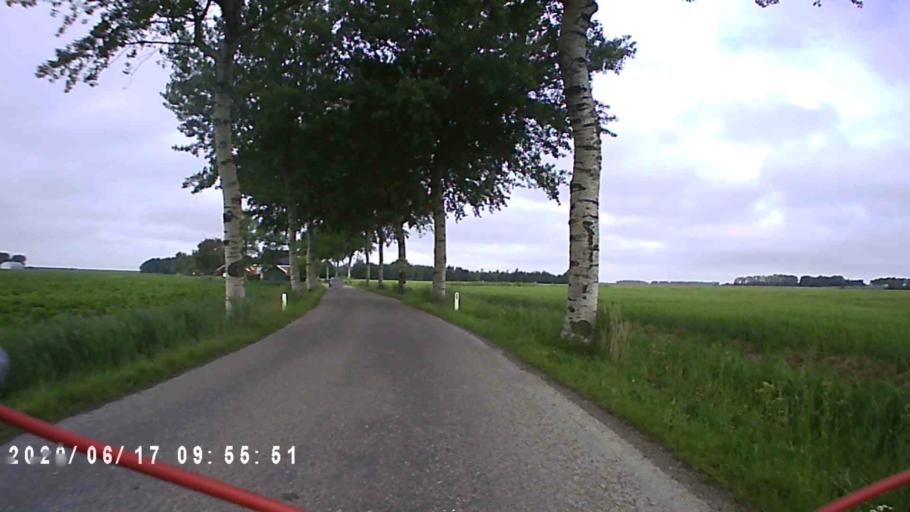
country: NL
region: Groningen
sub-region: Gemeente De Marne
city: Ulrum
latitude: 53.3596
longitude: 6.3030
